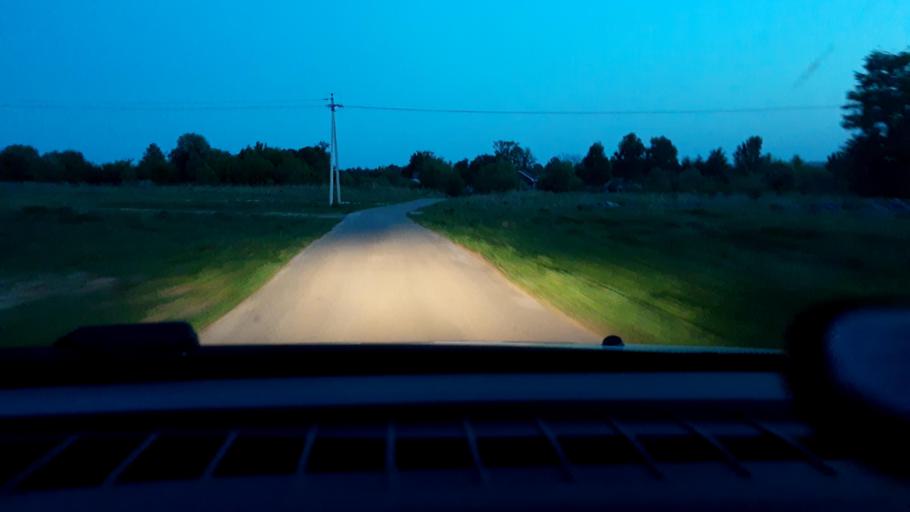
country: RU
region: Nizjnij Novgorod
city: Burevestnik
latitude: 56.0385
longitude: 43.7255
